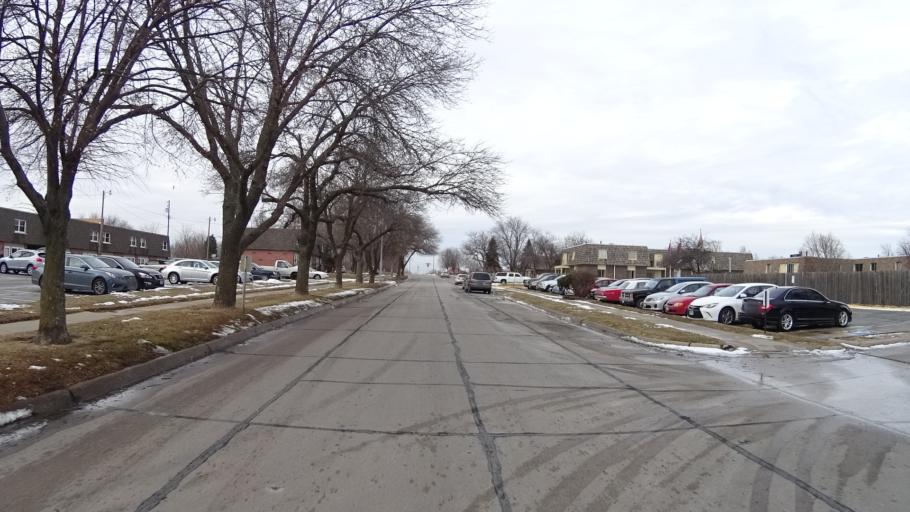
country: US
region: Nebraska
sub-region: Sarpy County
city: Bellevue
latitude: 41.1568
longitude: -95.9208
